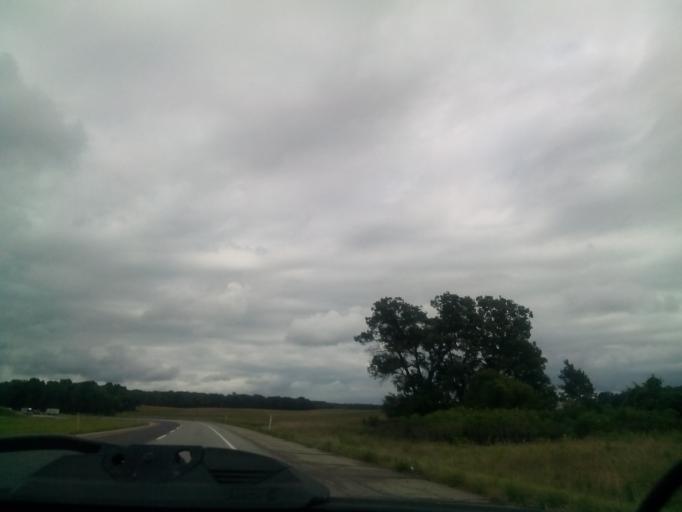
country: US
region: Michigan
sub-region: Saint Joseph County
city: Sturgis
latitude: 41.7396
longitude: -85.2844
